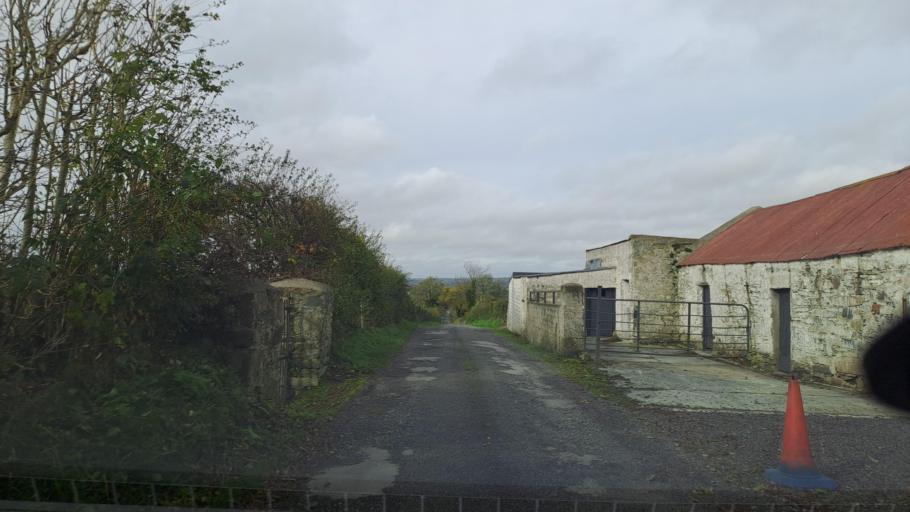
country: IE
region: Ulster
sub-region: County Monaghan
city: Carrickmacross
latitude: 54.0181
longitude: -6.8166
